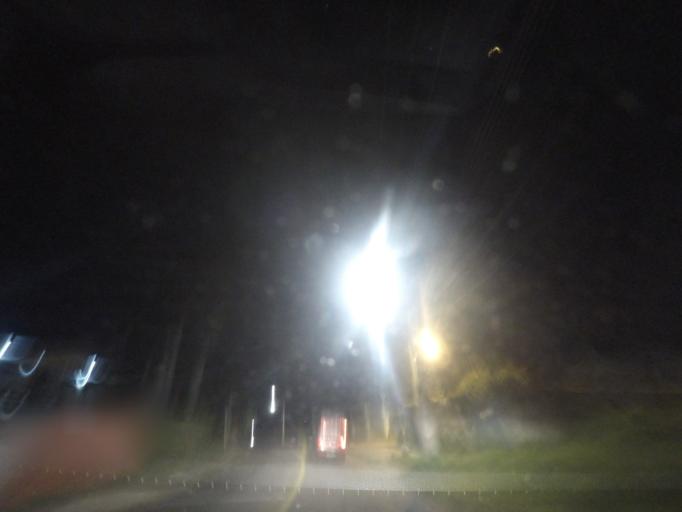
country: BR
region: Parana
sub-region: Almirante Tamandare
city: Almirante Tamandare
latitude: -25.3718
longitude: -49.2803
